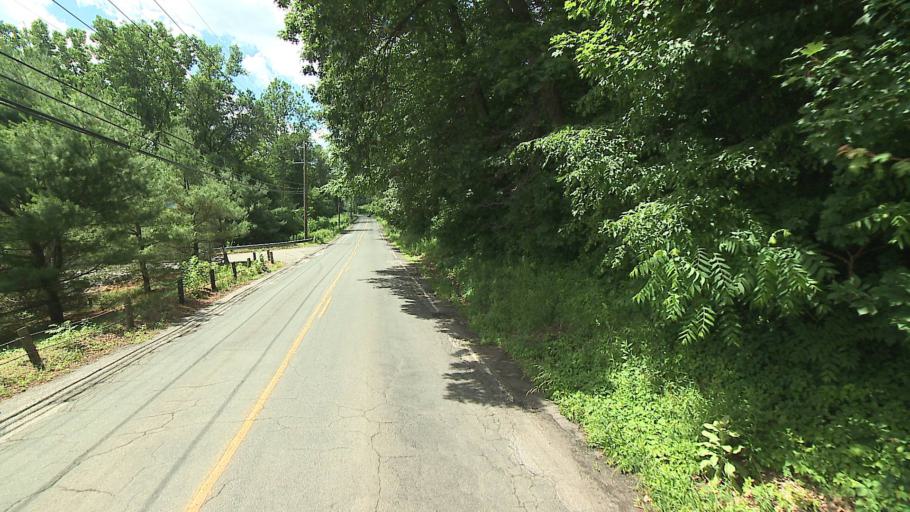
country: US
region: Connecticut
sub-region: Litchfield County
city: Kent
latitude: 41.7143
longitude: -73.4732
